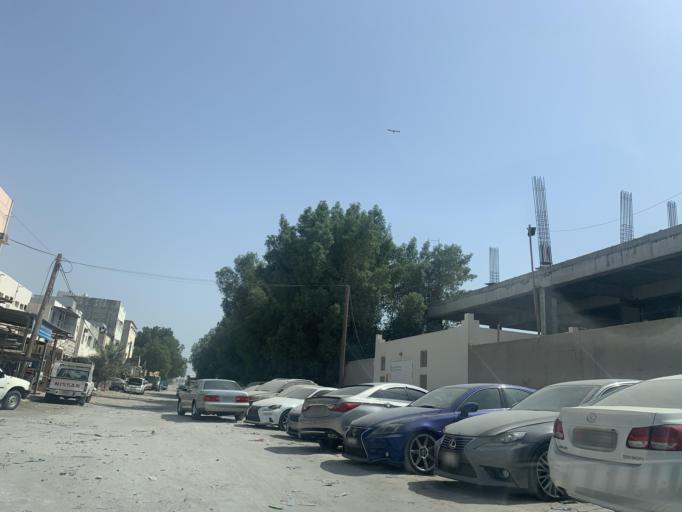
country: BH
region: Central Governorate
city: Madinat Hamad
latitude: 26.1382
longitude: 50.4839
